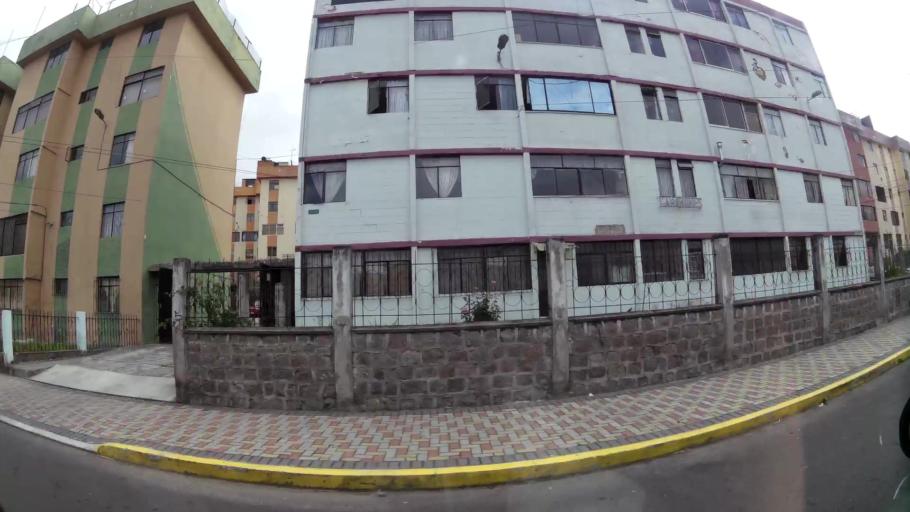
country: EC
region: Pichincha
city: Quito
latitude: -0.1346
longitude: -78.5008
